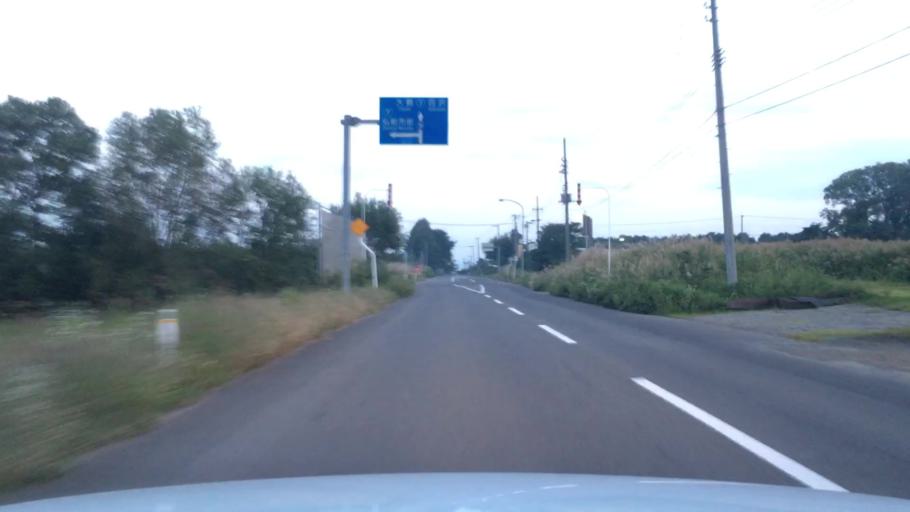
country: JP
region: Aomori
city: Hirosaki
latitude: 40.6787
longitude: 140.3730
